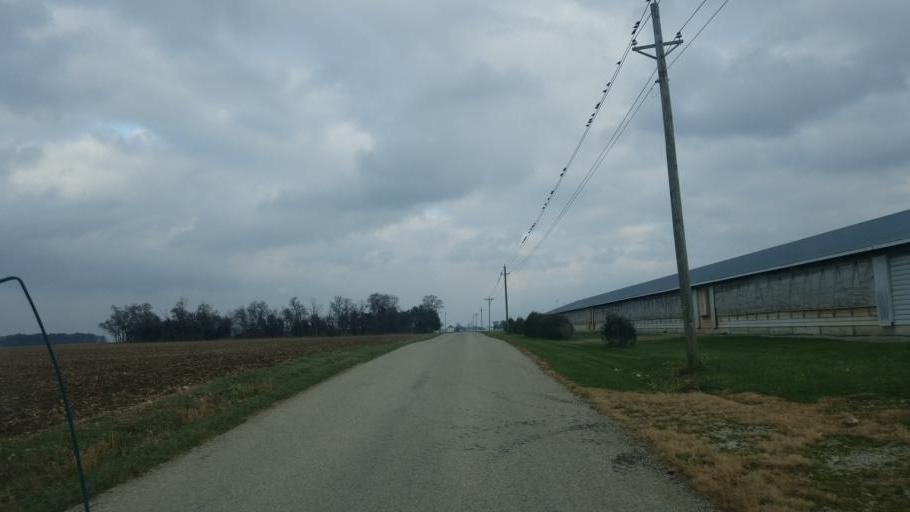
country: US
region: Ohio
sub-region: Mercer County
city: Fort Recovery
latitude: 40.5134
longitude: -84.8386
